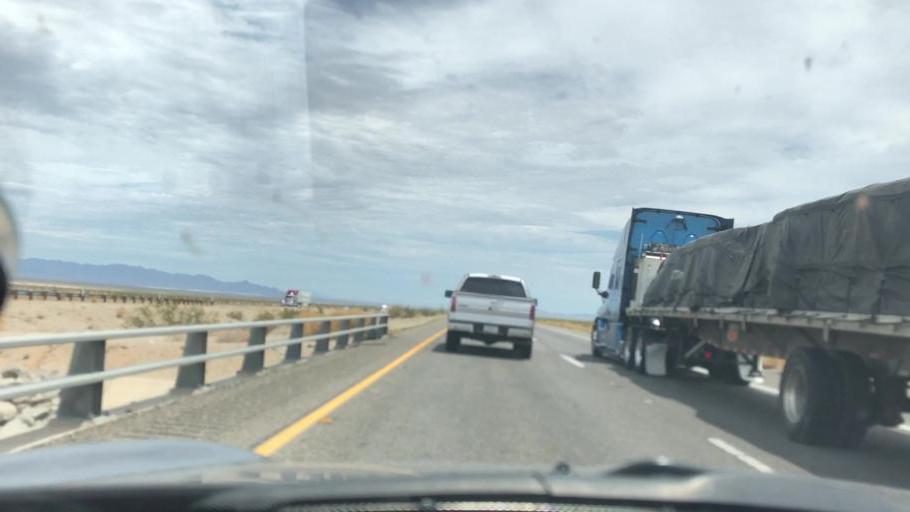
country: US
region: California
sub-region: Riverside County
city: Mesa Verde
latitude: 33.6708
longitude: -115.2045
